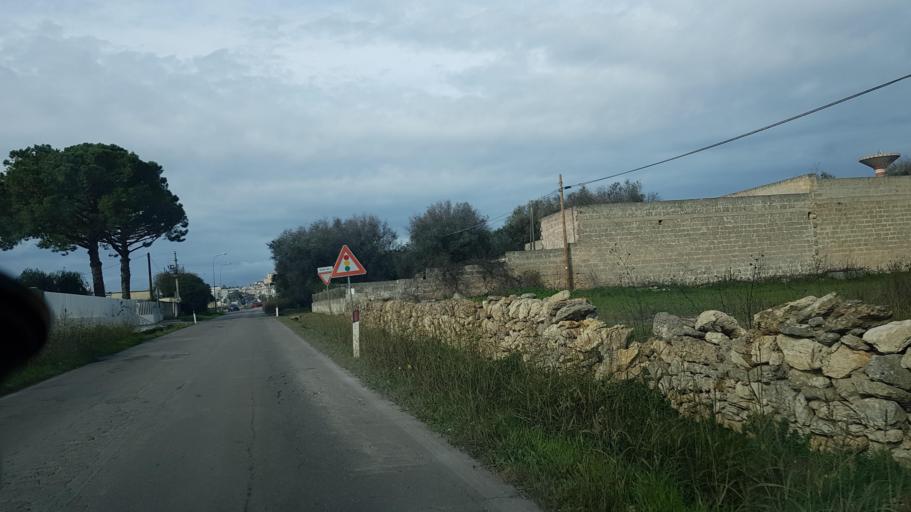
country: IT
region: Apulia
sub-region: Provincia di Brindisi
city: Oria
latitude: 40.4916
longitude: 17.6579
